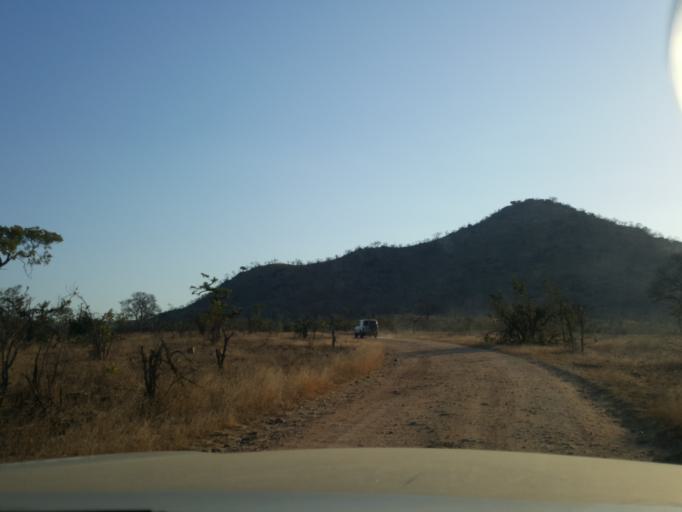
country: SZ
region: Hhohho
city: Ntfonjeni
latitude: -25.4250
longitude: 31.4391
